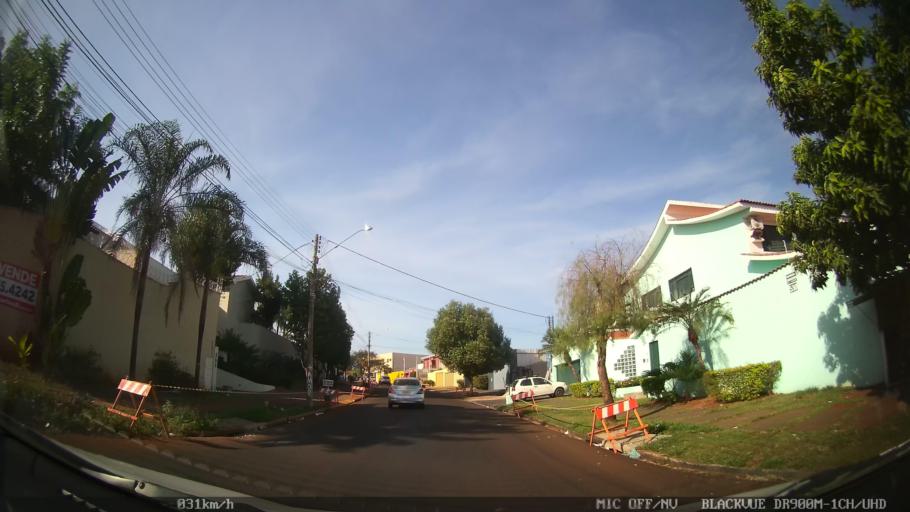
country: BR
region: Sao Paulo
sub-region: Ribeirao Preto
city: Ribeirao Preto
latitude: -21.1996
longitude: -47.8184
